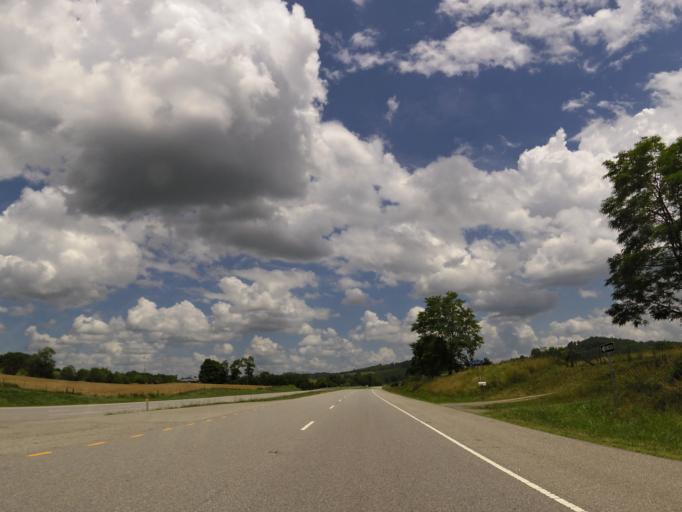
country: US
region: Tennessee
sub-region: Claiborne County
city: Harrogate
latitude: 36.6314
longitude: -83.4801
